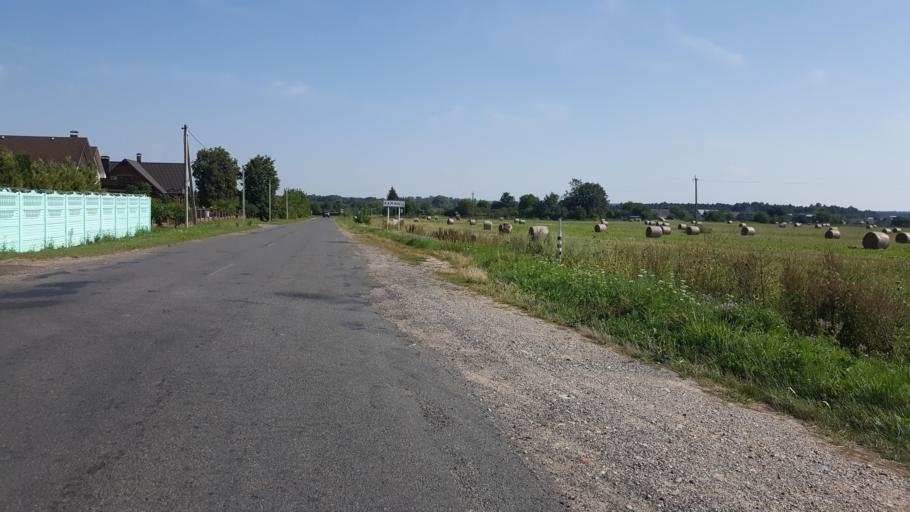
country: BY
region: Brest
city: Kamyanyets
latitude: 52.4092
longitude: 23.7933
